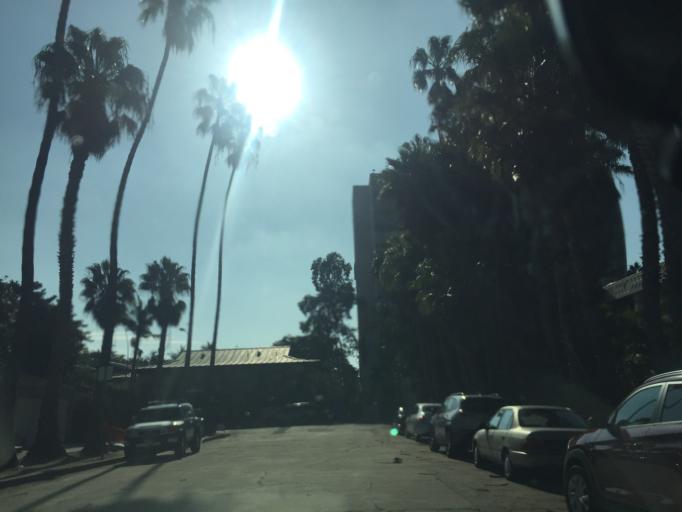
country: US
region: California
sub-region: San Diego County
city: La Jolla
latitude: 32.7913
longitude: -117.2519
